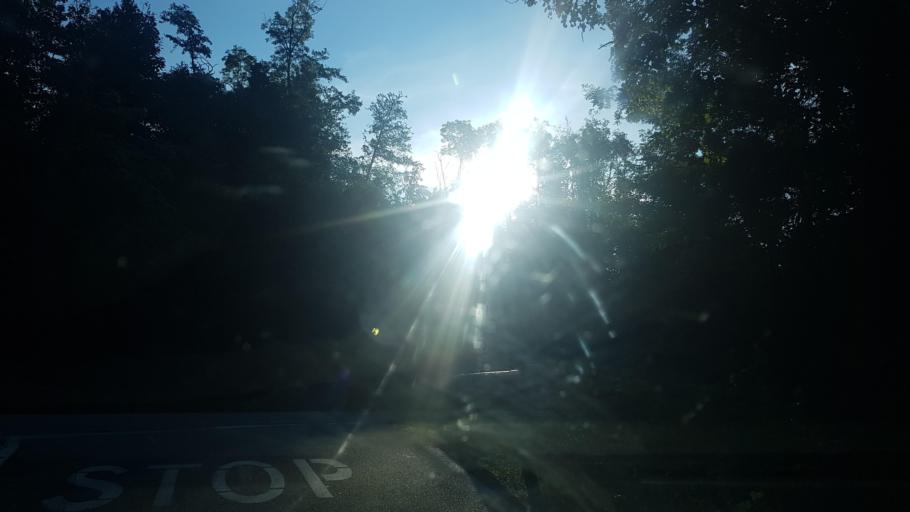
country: IT
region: Piedmont
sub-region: Provincia Verbano-Cusio-Ossola
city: Vignone
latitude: 45.9603
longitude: 8.5698
